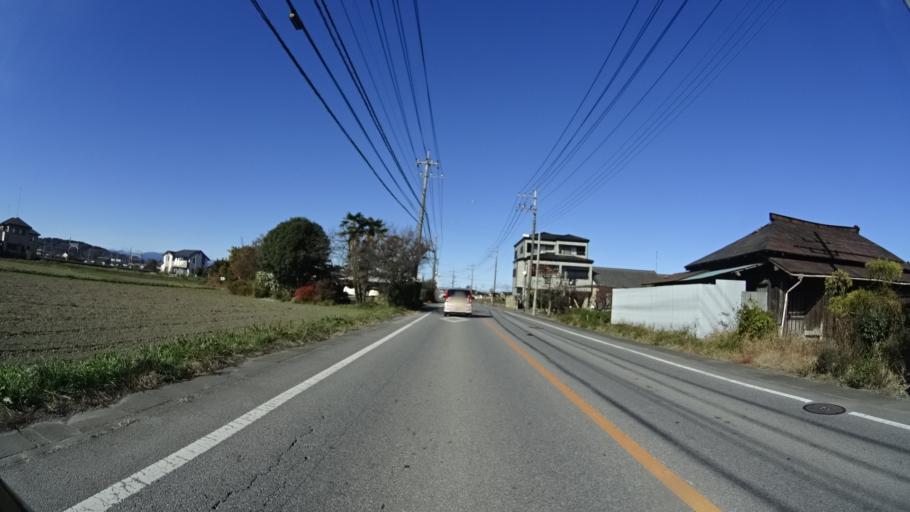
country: JP
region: Tochigi
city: Mibu
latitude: 36.4605
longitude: 139.7531
